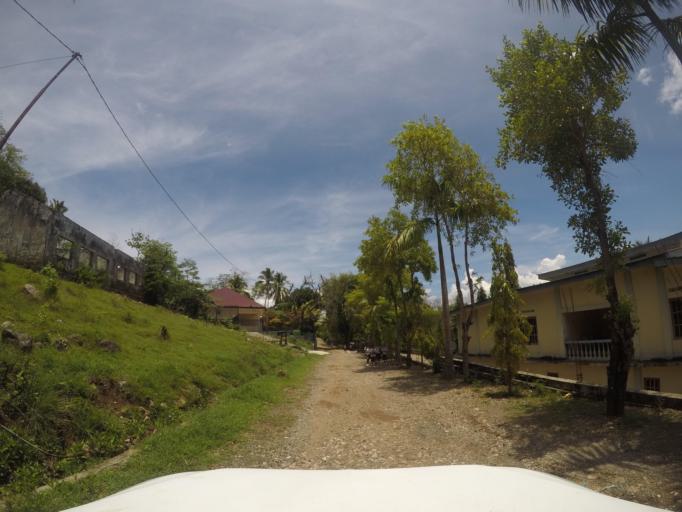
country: TL
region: Bobonaro
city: Maliana
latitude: -8.9968
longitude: 125.2213
